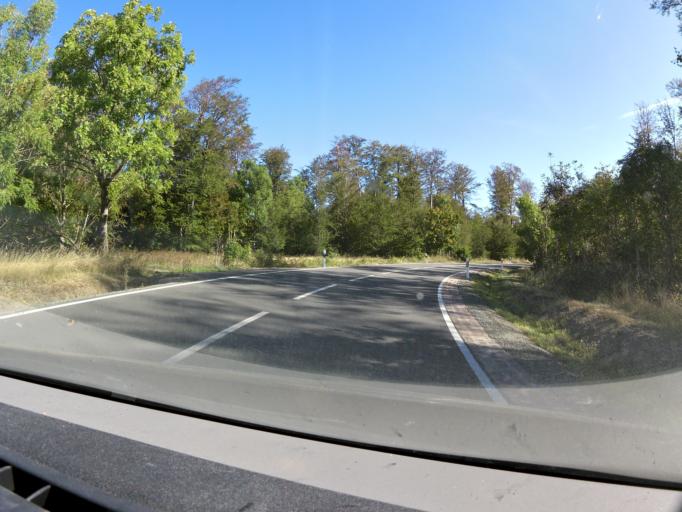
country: DE
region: Saxony-Anhalt
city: Hasselfelde
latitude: 51.6782
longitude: 10.9005
